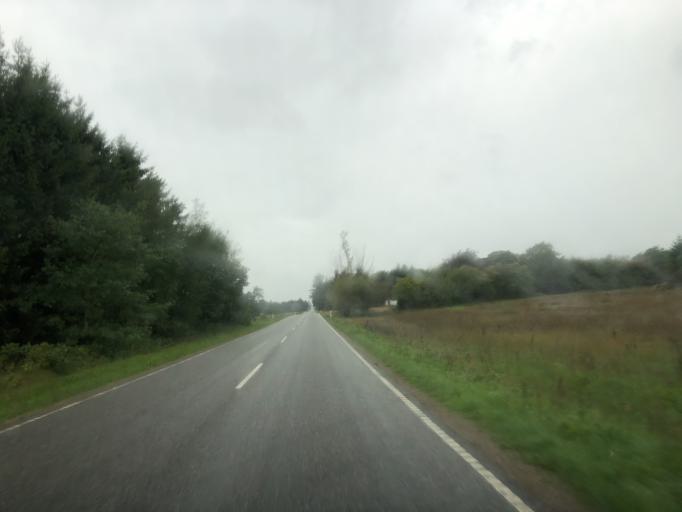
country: DK
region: South Denmark
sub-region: Vejle Kommune
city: Give
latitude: 55.9838
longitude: 9.2700
